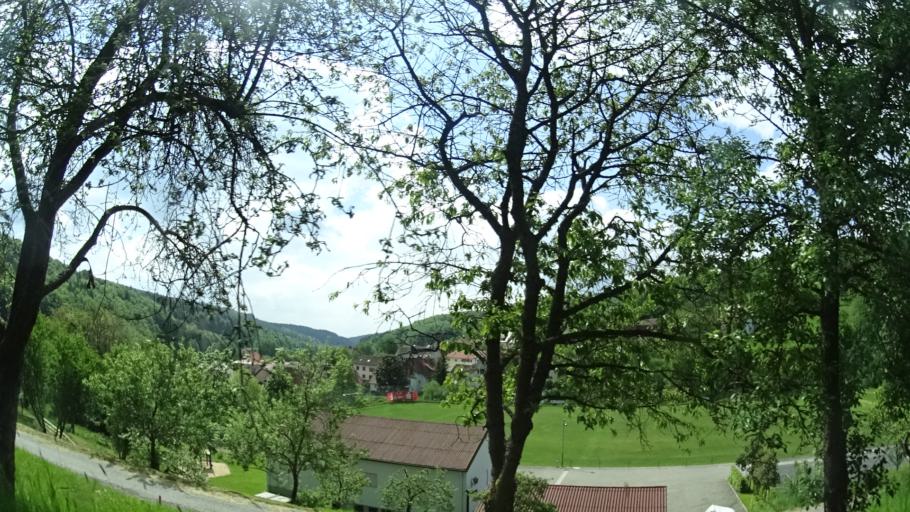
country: DE
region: Bavaria
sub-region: Regierungsbezirk Unterfranken
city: Sandberg
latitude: 50.3399
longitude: 10.0366
